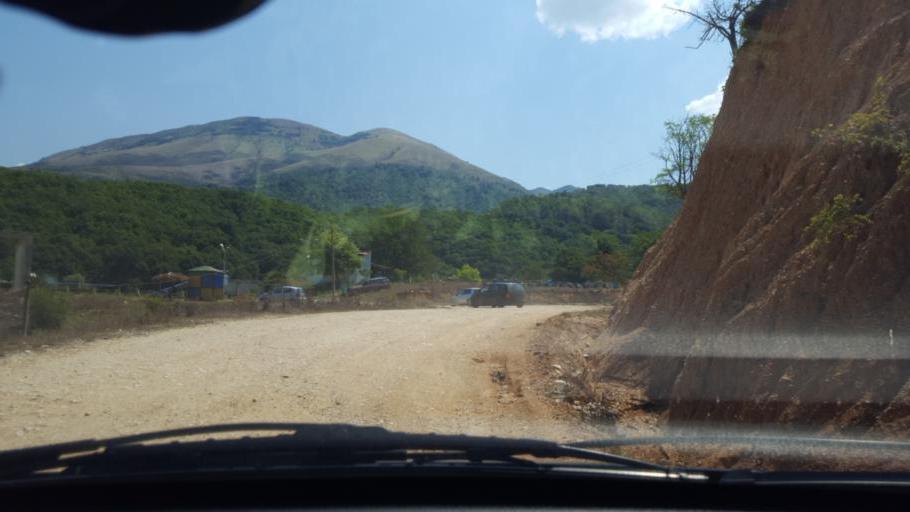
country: AL
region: Vlore
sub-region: Rrethi i Sarandes
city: Dhiver
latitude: 39.9172
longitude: 20.1848
